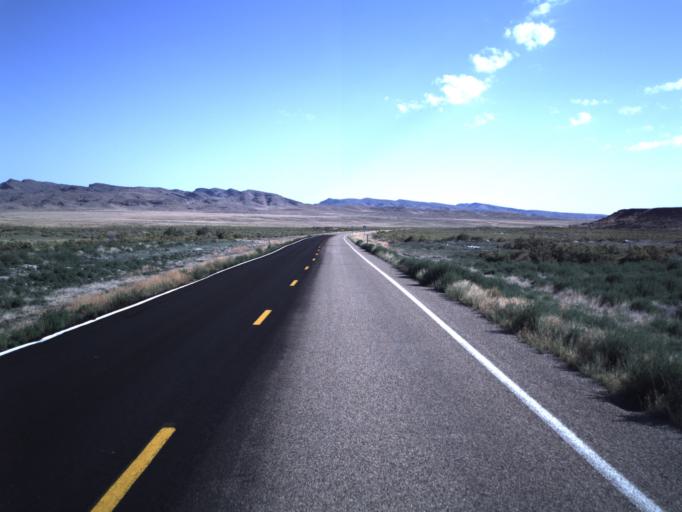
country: US
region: Utah
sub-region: Beaver County
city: Milford
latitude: 38.7181
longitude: -112.9687
